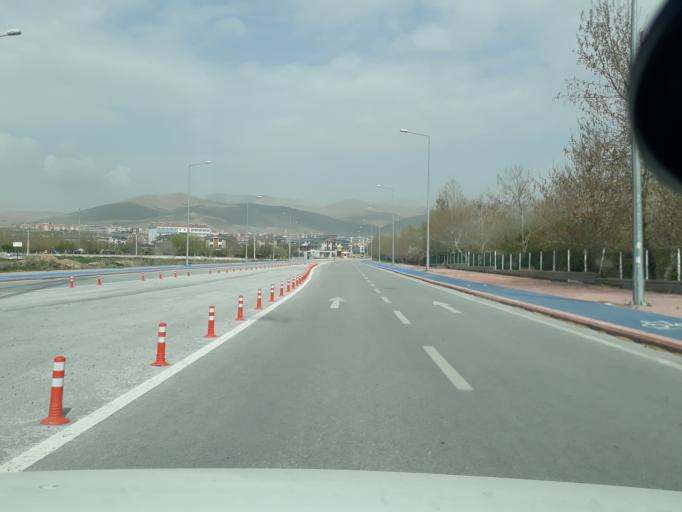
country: TR
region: Konya
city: Sille
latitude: 37.9474
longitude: 32.4786
